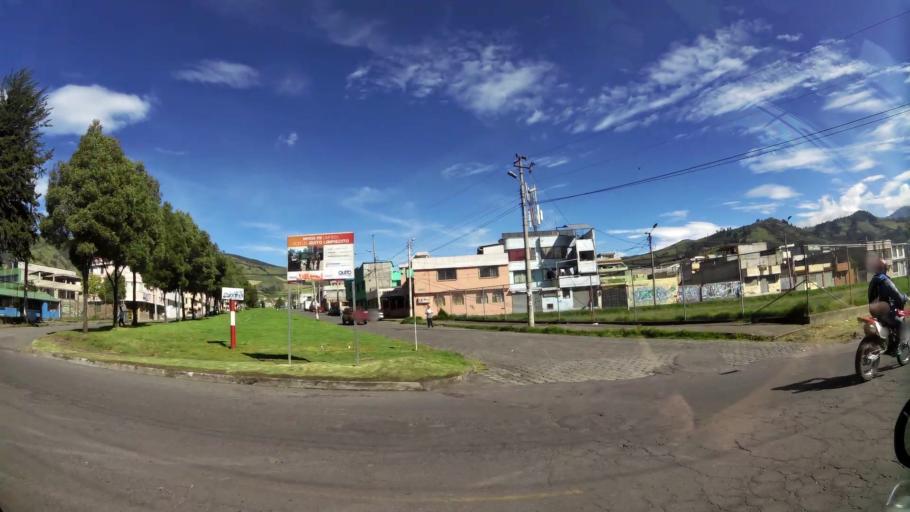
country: EC
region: Pichincha
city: Quito
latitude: -0.2911
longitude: -78.5617
